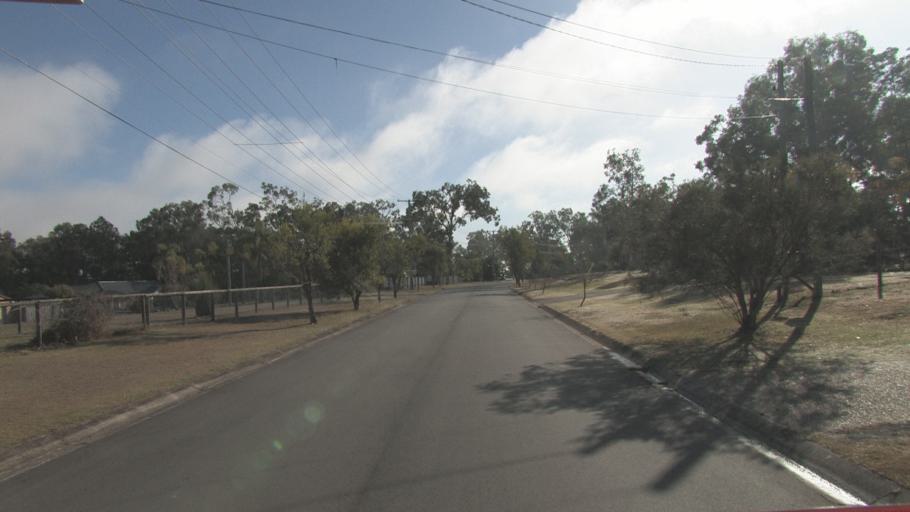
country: AU
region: Queensland
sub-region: Logan
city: Park Ridge South
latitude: -27.6965
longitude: 153.0325
